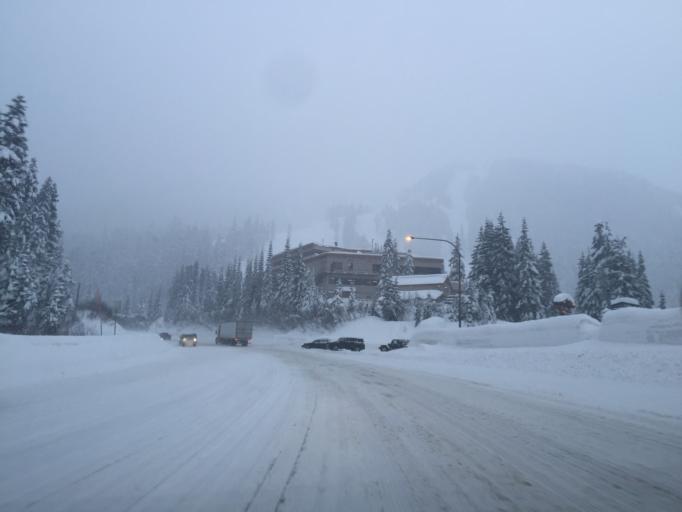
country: US
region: Washington
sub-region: Chelan County
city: Leavenworth
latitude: 47.7452
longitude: -121.0928
